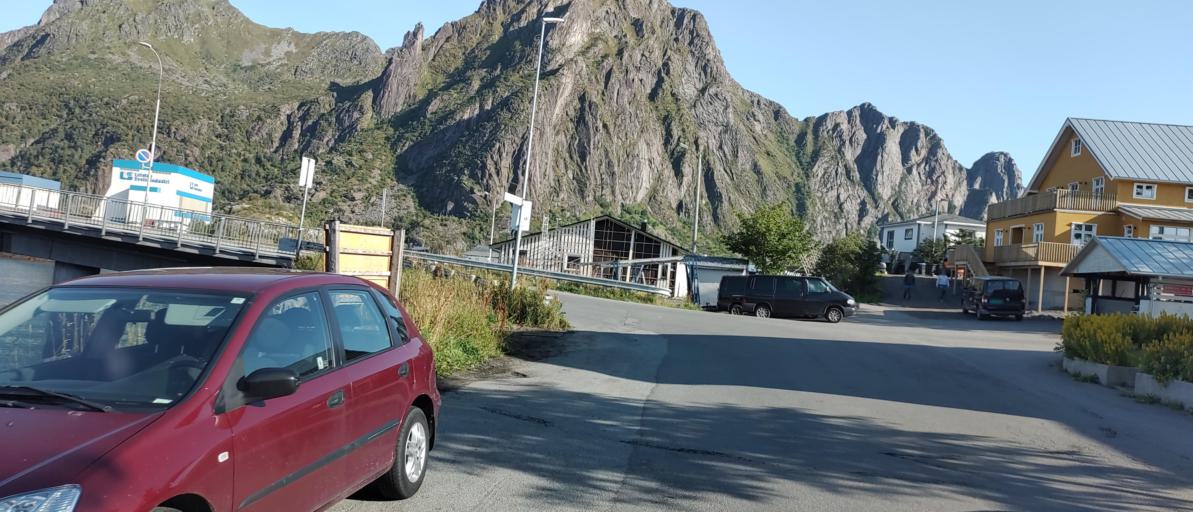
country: NO
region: Nordland
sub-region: Vagan
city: Svolvaer
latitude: 68.2345
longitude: 14.5801
